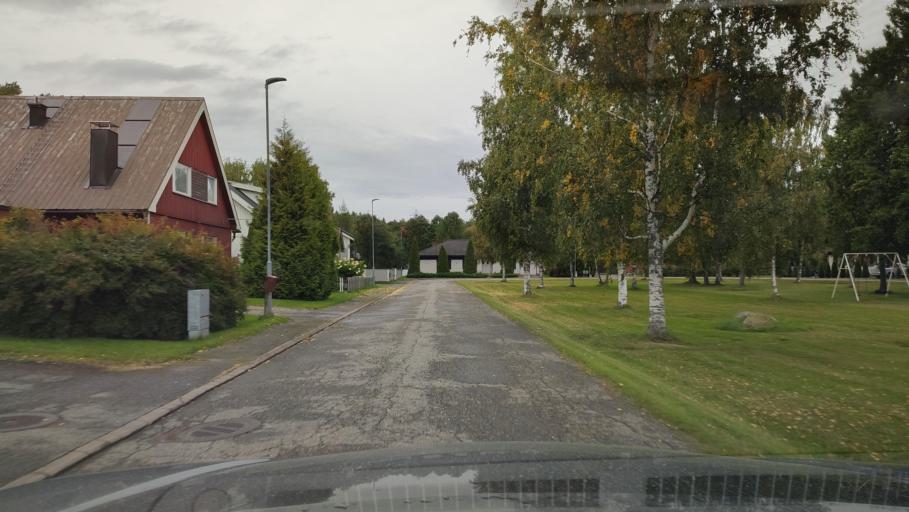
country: FI
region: Ostrobothnia
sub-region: Sydosterbotten
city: Kristinestad
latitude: 62.2821
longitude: 21.3589
